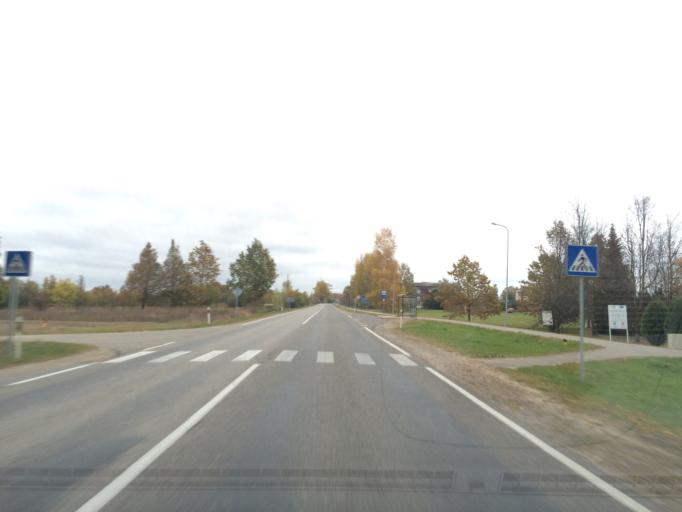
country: LV
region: Jekabpils Rajons
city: Jekabpils
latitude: 56.5155
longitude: 25.9405
